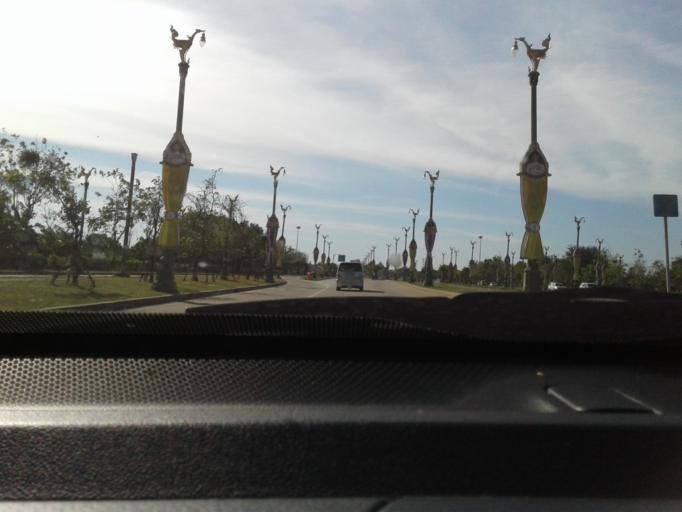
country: TH
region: Bangkok
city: Thawi Watthana
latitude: 13.7770
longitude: 100.3315
